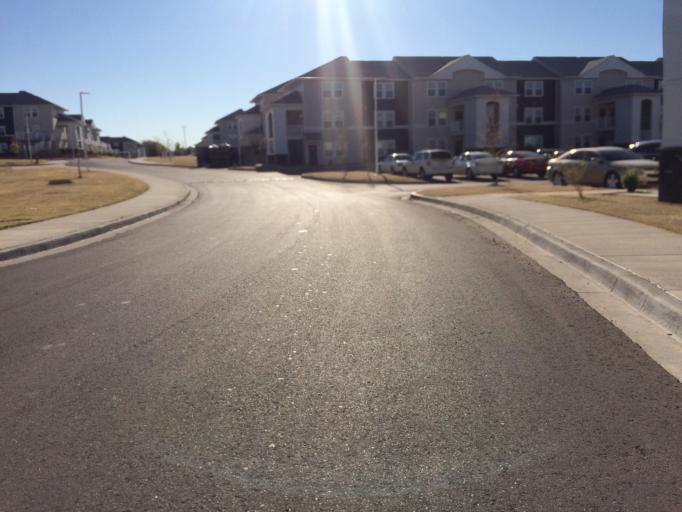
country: US
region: Oklahoma
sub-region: Cleveland County
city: Noble
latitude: 35.1775
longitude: -97.4207
